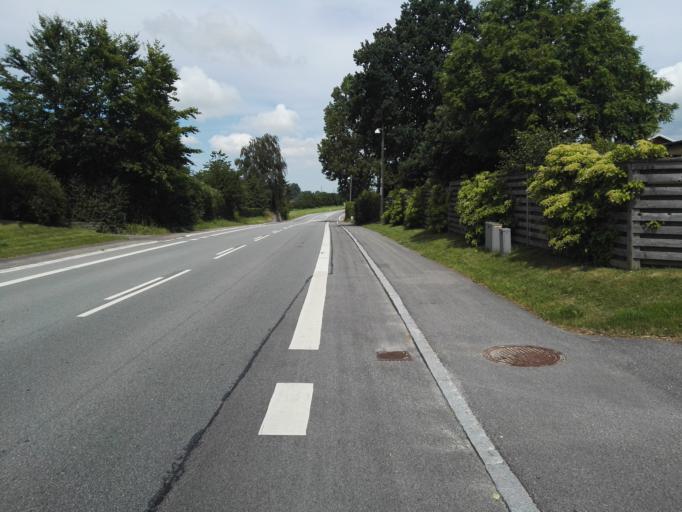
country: DK
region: Capital Region
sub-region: Frederikssund Kommune
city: Slangerup
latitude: 55.8554
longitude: 12.1733
